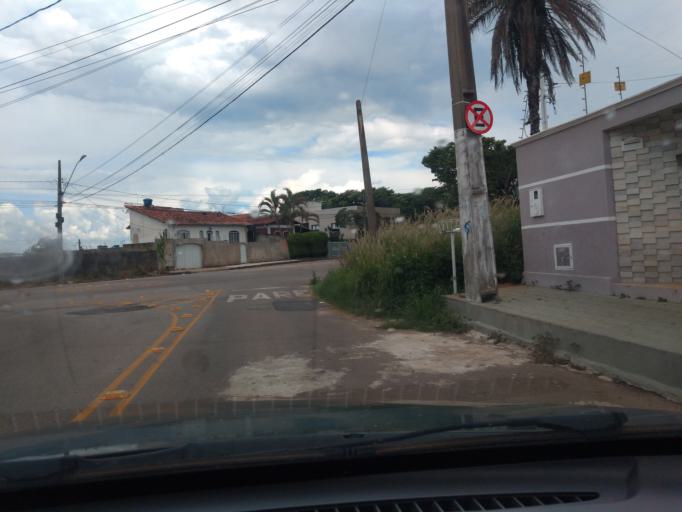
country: BR
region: Minas Gerais
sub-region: Tres Coracoes
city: Tres Coracoes
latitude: -21.6864
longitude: -45.2645
